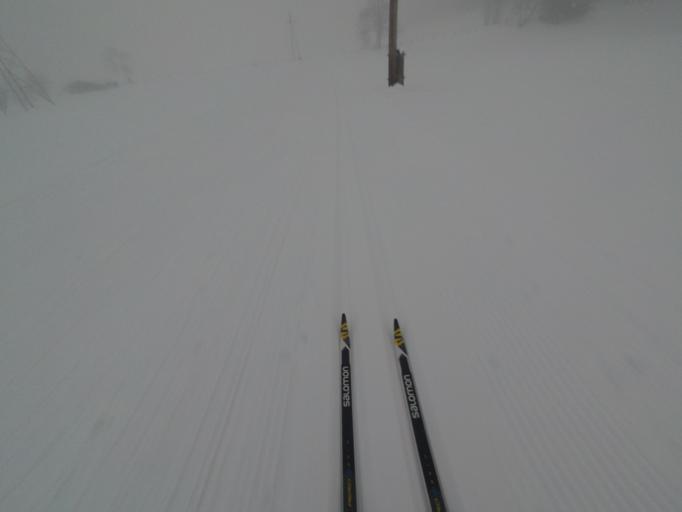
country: AT
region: Salzburg
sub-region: Politischer Bezirk Sankt Johann im Pongau
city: Wagrain
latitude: 47.3541
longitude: 13.3292
